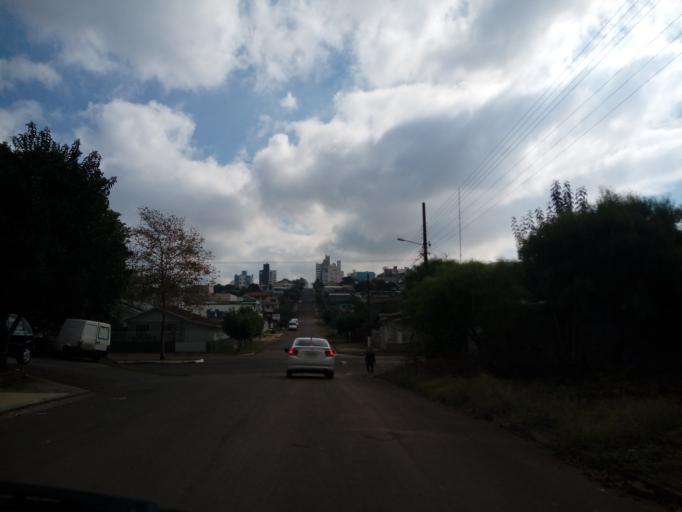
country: BR
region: Santa Catarina
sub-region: Chapeco
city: Chapeco
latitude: -27.0970
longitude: -52.5984
